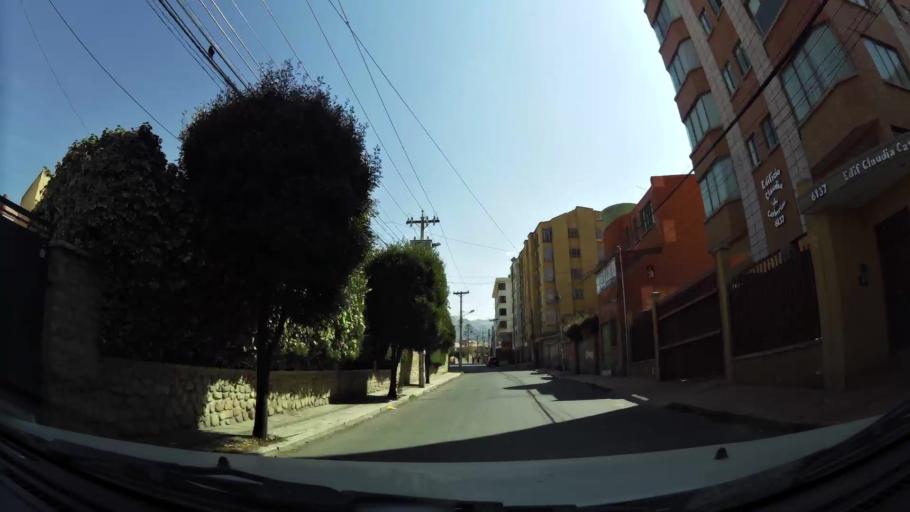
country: BO
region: La Paz
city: La Paz
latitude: -16.5177
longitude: -68.0859
